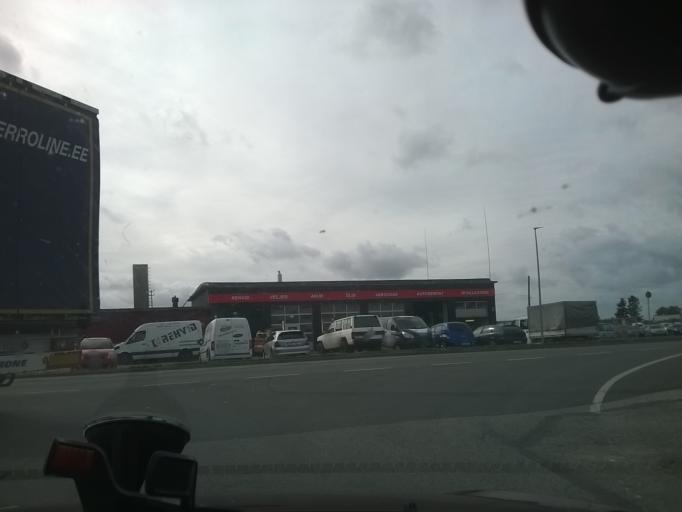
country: EE
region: Harju
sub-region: Rae vald
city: Jueri
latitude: 59.3819
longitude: 24.8315
